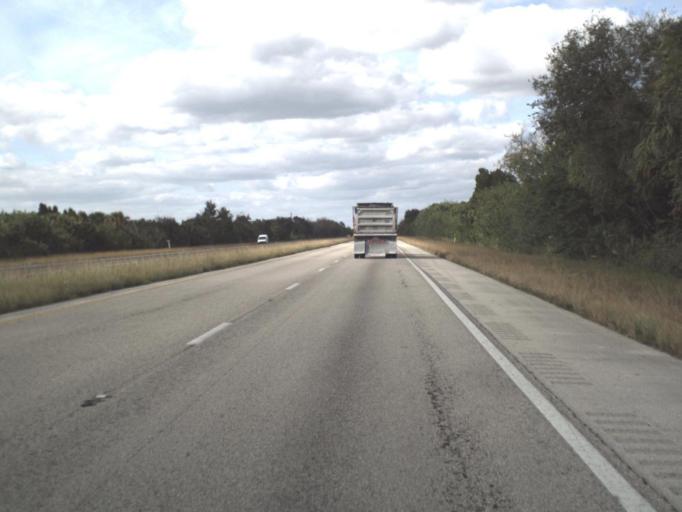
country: US
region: Florida
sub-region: Brevard County
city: Port Saint John
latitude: 28.4178
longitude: -80.8429
